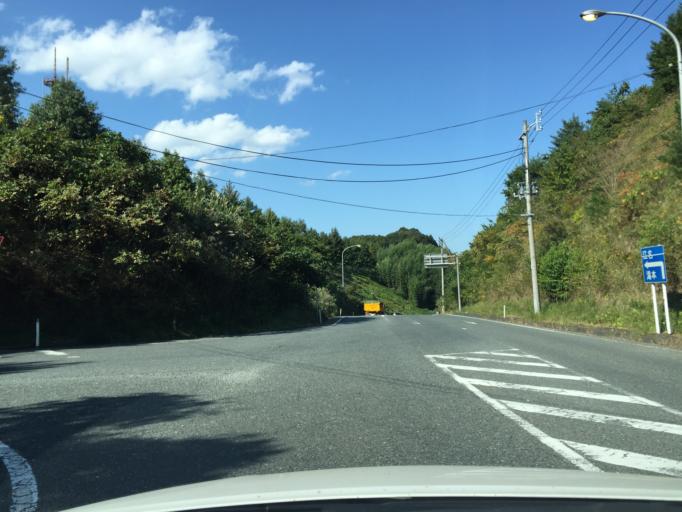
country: JP
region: Fukushima
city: Iwaki
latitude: 36.9986
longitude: 140.8980
